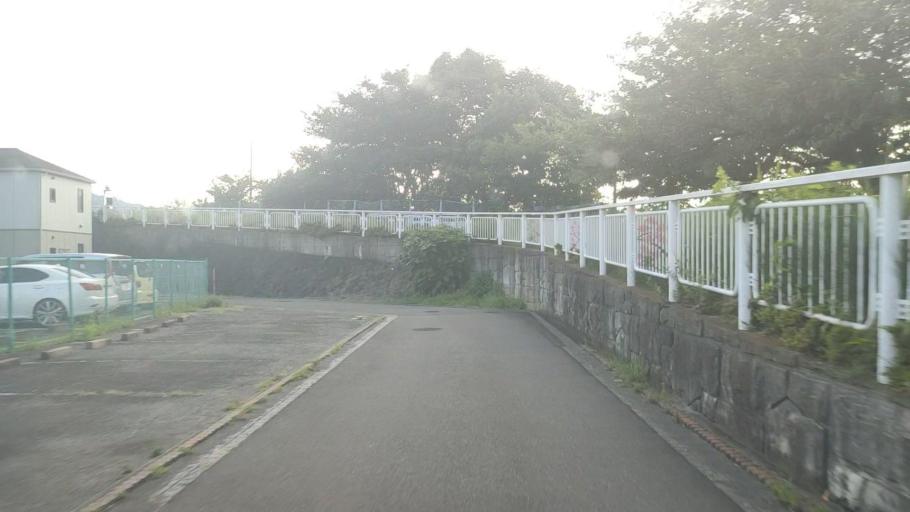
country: JP
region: Kanagawa
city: Hiratsuka
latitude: 35.3348
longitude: 139.3227
